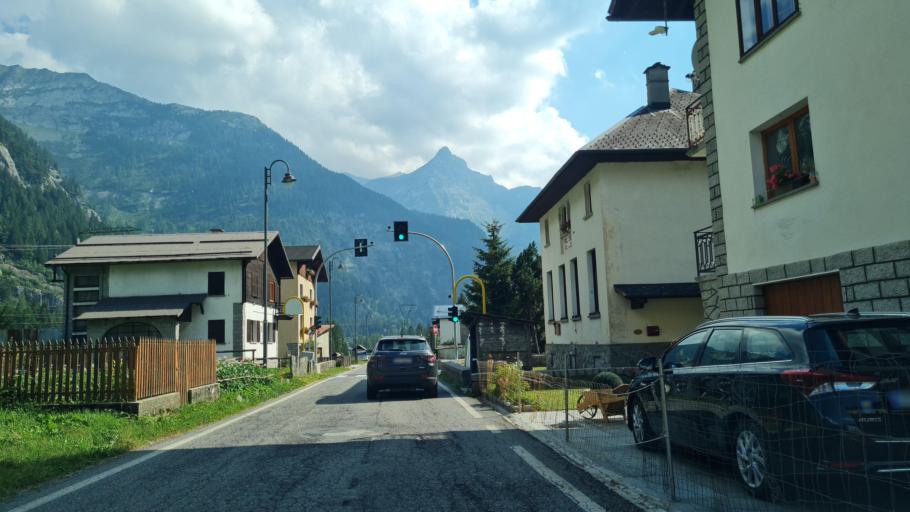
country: IT
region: Piedmont
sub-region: Provincia Verbano-Cusio-Ossola
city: Formazza
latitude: 46.3533
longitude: 8.4279
